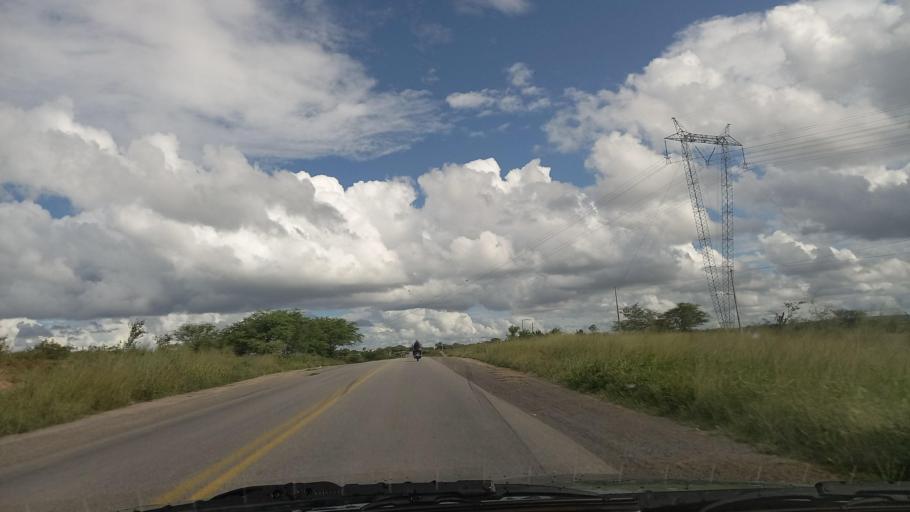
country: BR
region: Pernambuco
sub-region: Lajedo
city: Lajedo
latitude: -8.6000
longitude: -36.2923
